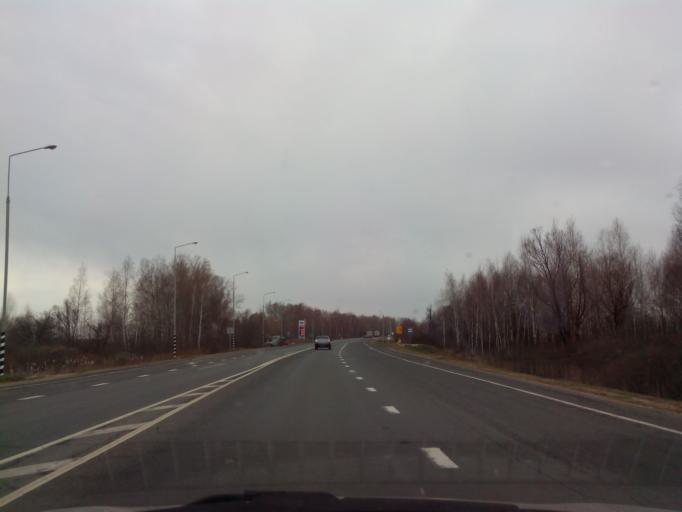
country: RU
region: Tambov
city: Pervomayskiy
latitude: 53.0851
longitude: 40.4049
